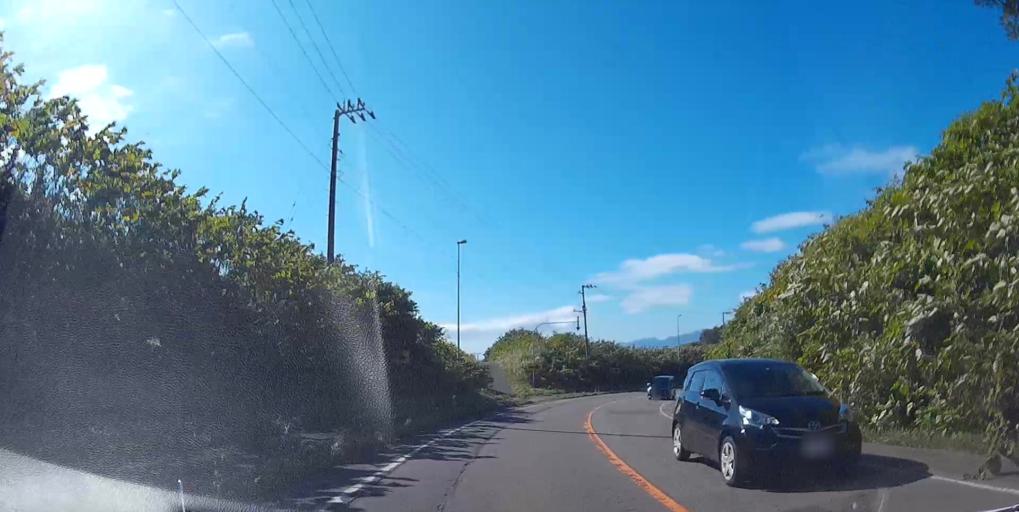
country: JP
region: Hokkaido
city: Kamiiso
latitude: 42.0176
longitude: 140.1041
